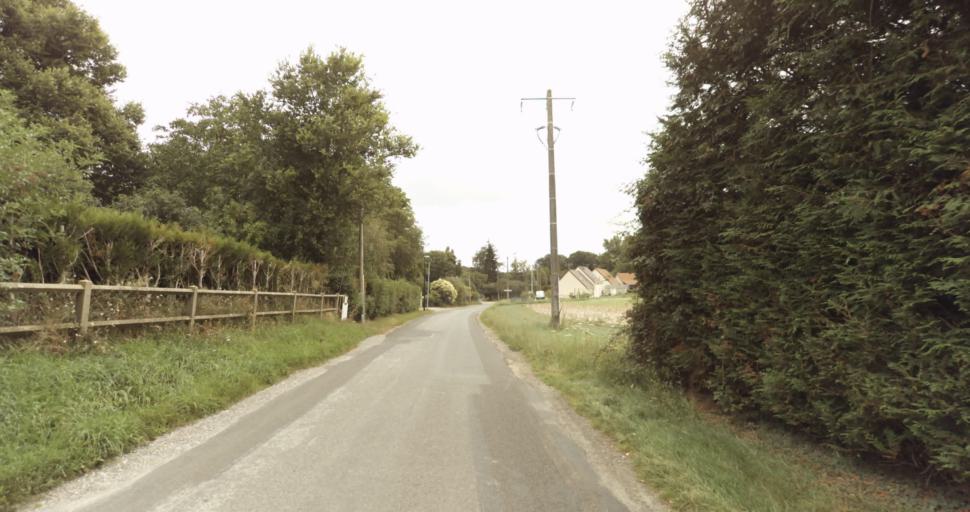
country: FR
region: Haute-Normandie
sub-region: Departement de l'Eure
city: Pacy-sur-Eure
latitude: 48.9509
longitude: 1.3541
